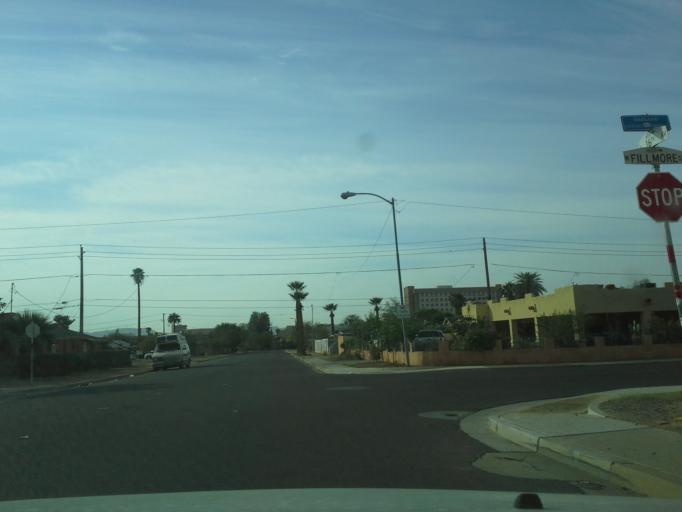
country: US
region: Arizona
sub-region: Maricopa County
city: Phoenix
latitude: 33.4552
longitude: -112.0935
